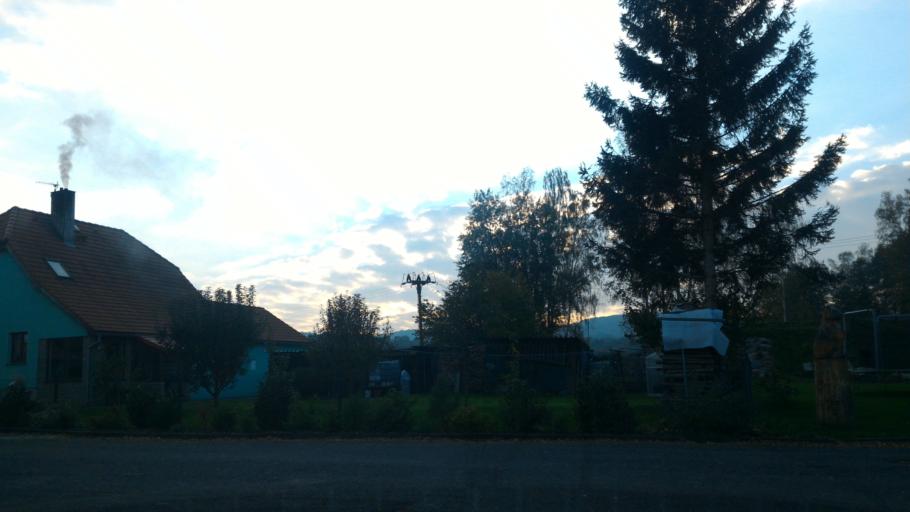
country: DE
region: Saxony
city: Seifhennersdorf
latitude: 50.9199
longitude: 14.6030
